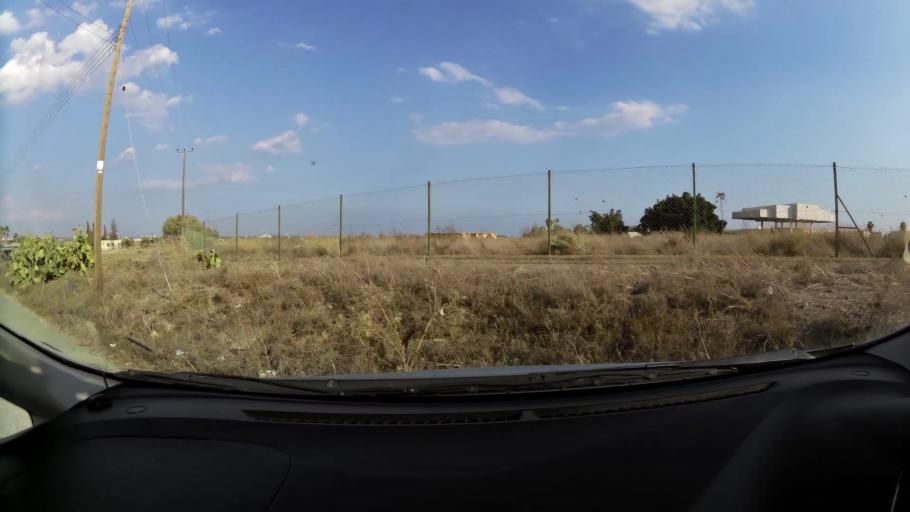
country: CY
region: Larnaka
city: Dhromolaxia
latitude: 34.8852
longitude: 33.5944
